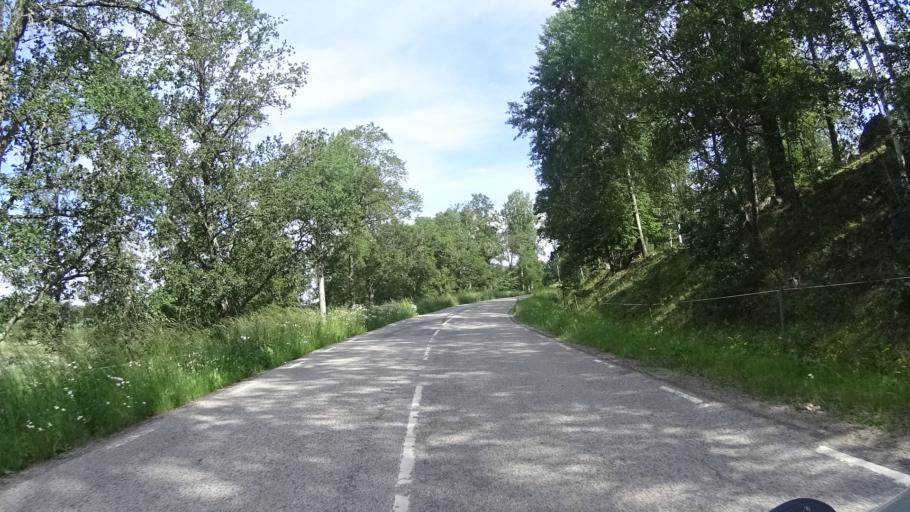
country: SE
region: Kalmar
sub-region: Vasterviks Kommun
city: Overum
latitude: 57.9007
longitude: 16.1725
